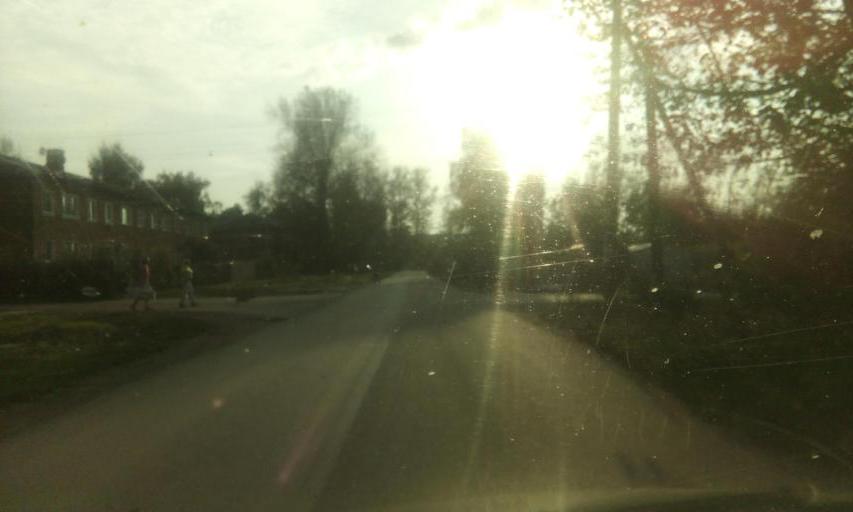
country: RU
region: Tula
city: Partizan
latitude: 53.9240
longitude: 38.0960
